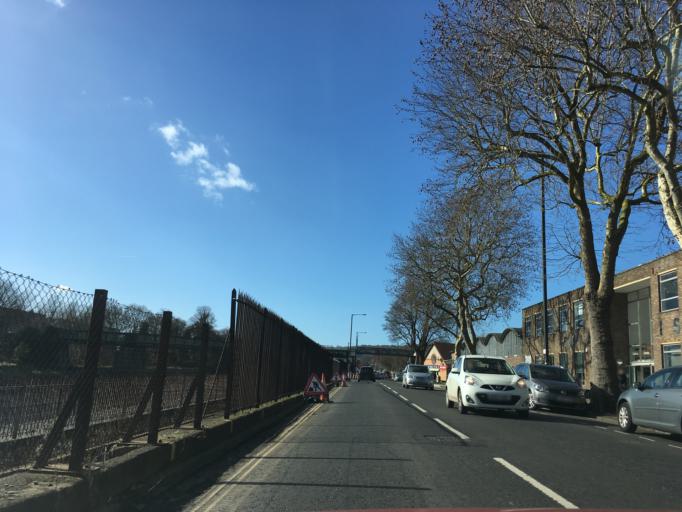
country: GB
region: England
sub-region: Bristol
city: Bristol
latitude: 51.4468
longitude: -2.6099
